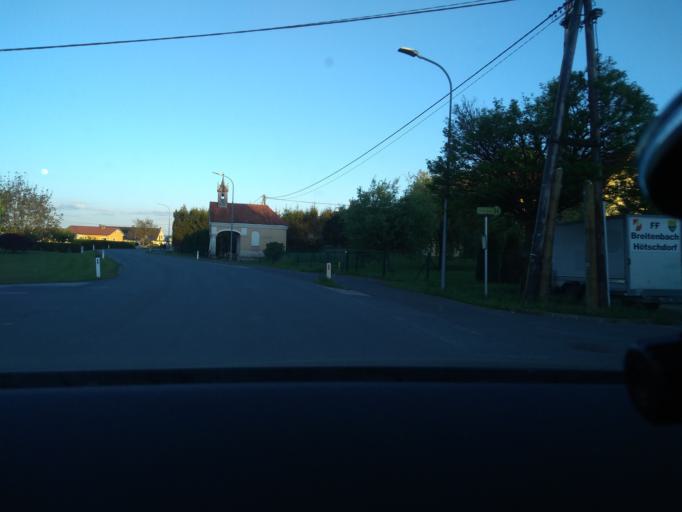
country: AT
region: Styria
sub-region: Politischer Bezirk Deutschlandsberg
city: Lannach
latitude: 46.9600
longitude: 15.3184
